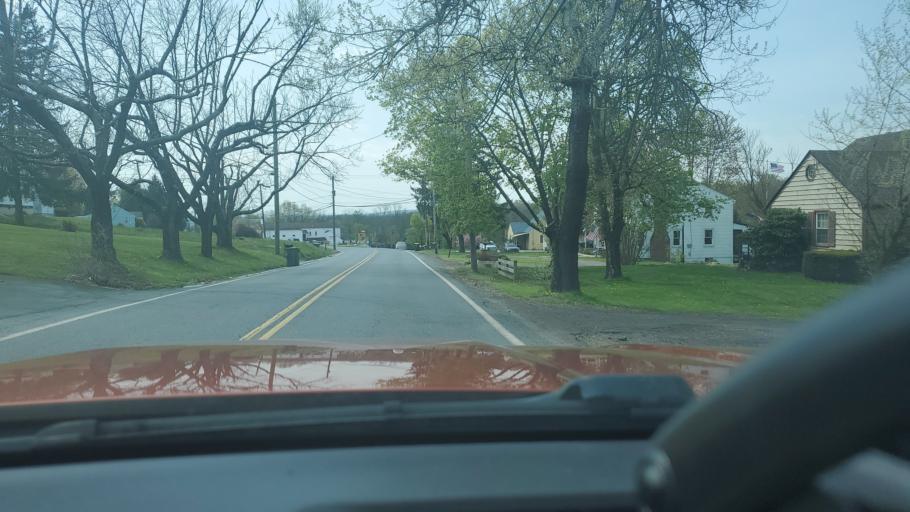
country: US
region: Pennsylvania
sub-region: Montgomery County
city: Halfway House
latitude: 40.2817
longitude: -75.6421
